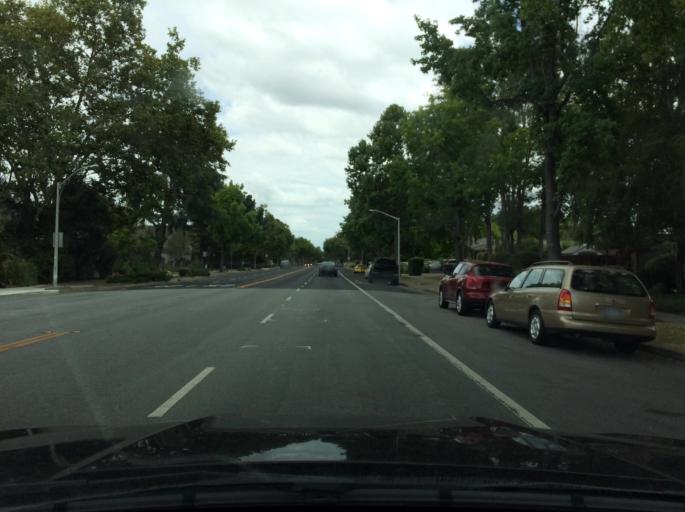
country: US
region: California
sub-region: Santa Clara County
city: Palo Alto
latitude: 37.4275
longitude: -122.1199
